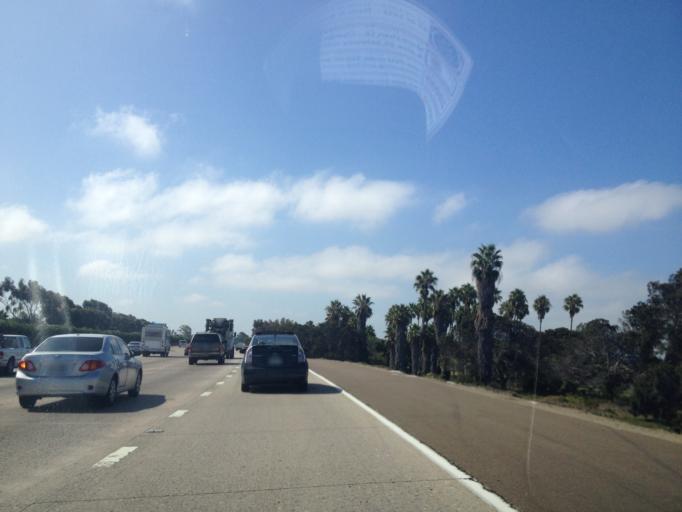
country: US
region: California
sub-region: San Diego County
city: San Diego
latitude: 32.7777
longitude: -117.2088
